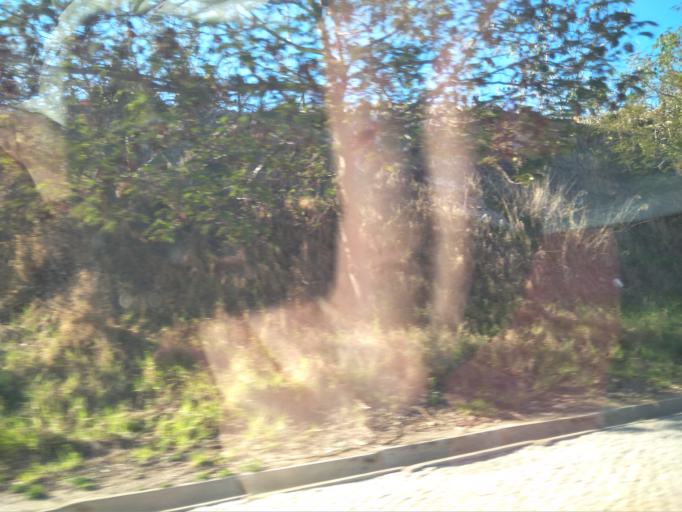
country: PT
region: Faro
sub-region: Albufeira
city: Albufeira
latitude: 37.0952
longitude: -8.2243
